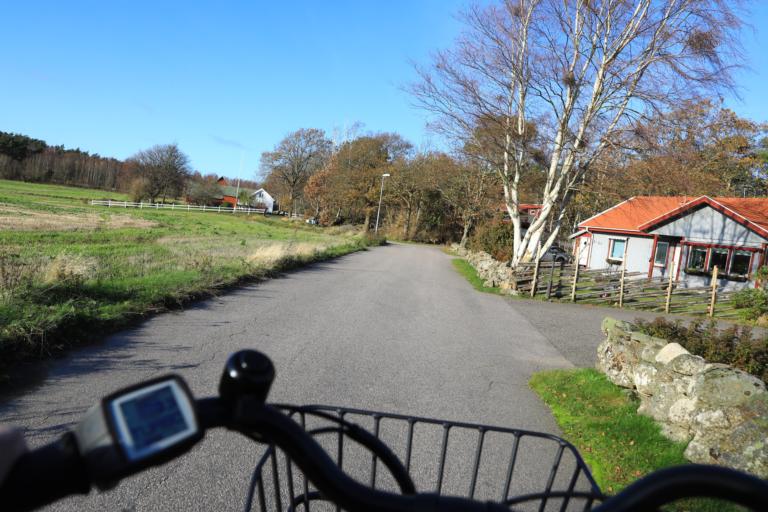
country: SE
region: Halland
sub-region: Varbergs Kommun
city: Varberg
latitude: 57.1732
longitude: 12.2198
